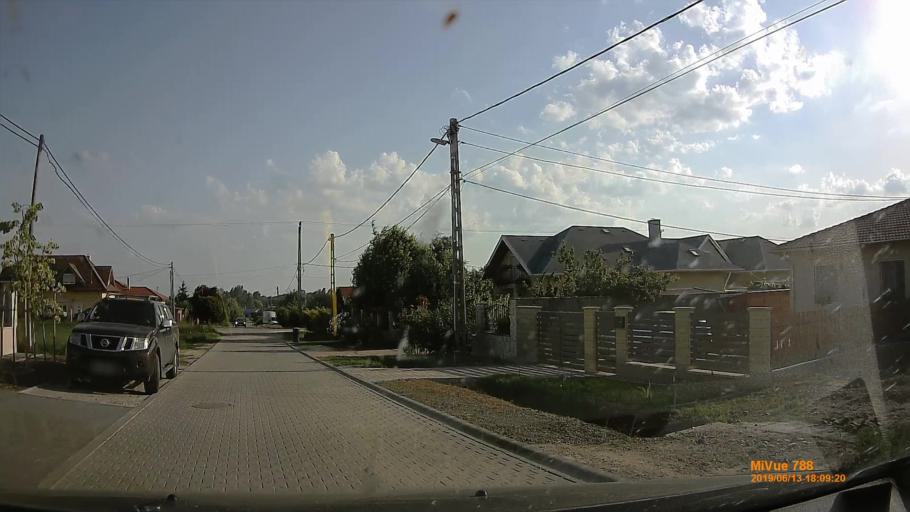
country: HU
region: Pest
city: Ecser
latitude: 47.4516
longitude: 19.3105
